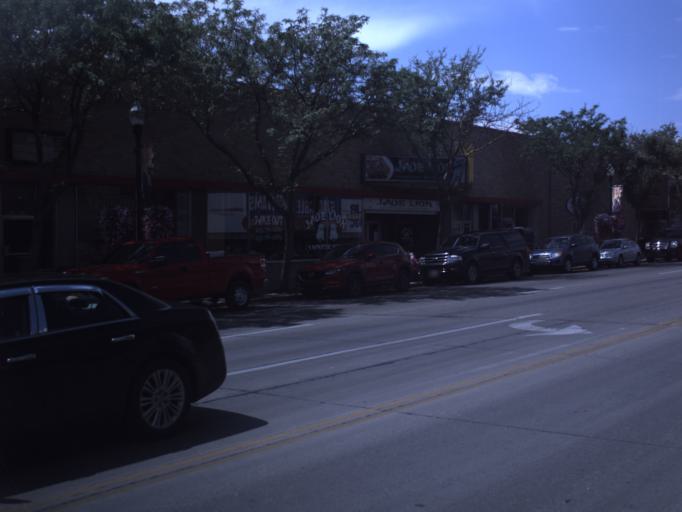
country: US
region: Utah
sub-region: Uintah County
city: Vernal
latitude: 40.4558
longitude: -109.5289
